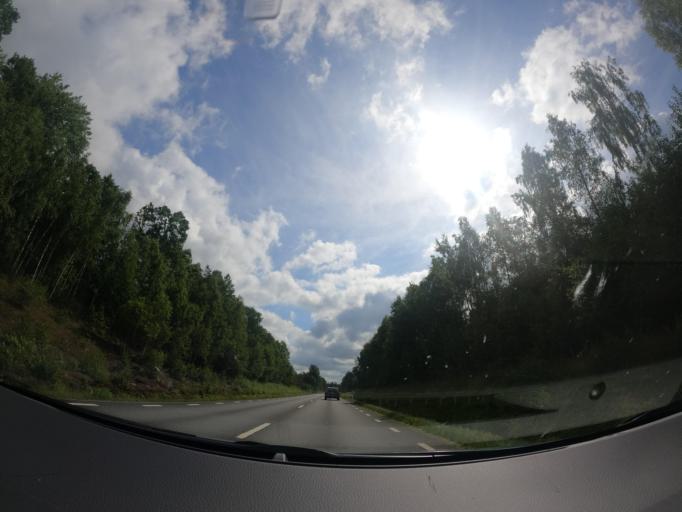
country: SE
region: Joenkoeping
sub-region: Gislaveds Kommun
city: Smalandsstenar
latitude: 57.1208
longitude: 13.3727
